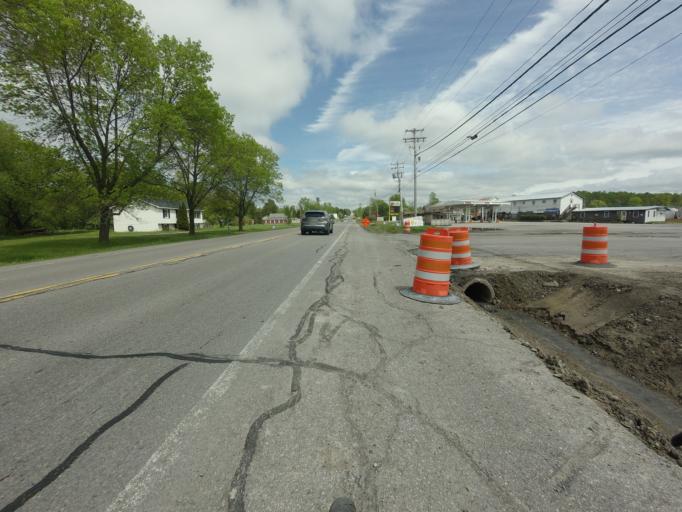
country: CA
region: Ontario
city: Cornwall
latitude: 44.9779
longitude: -74.7052
